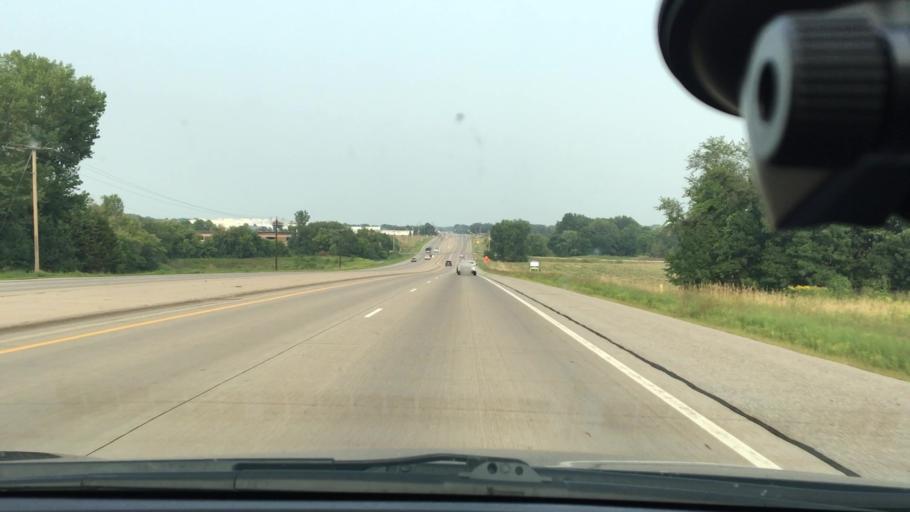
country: US
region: Minnesota
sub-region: Wright County
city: Saint Michael
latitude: 45.2115
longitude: -93.6350
